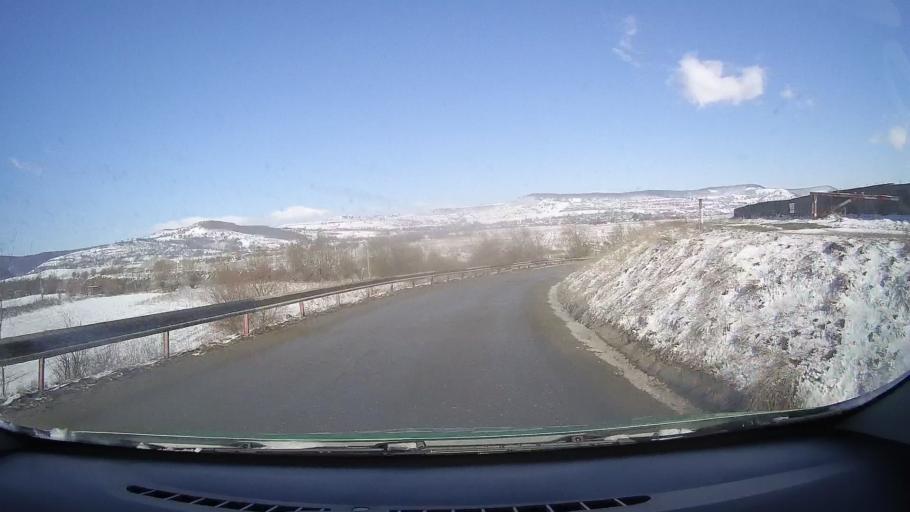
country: RO
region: Sibiu
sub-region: Comuna Avrig
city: Avrig
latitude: 45.7443
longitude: 24.3894
